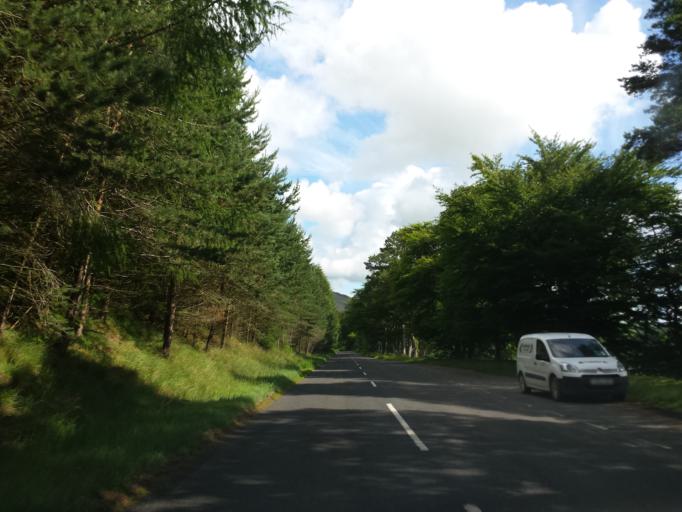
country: GB
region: Scotland
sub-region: The Scottish Borders
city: Peebles
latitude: 55.4803
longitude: -3.2084
